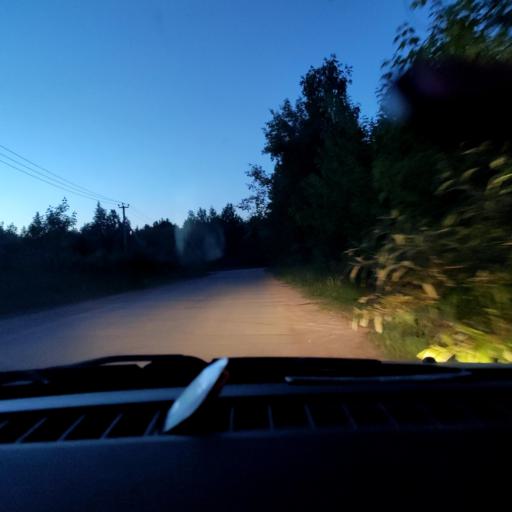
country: RU
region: Perm
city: Kultayevo
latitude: 57.9581
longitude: 55.9104
